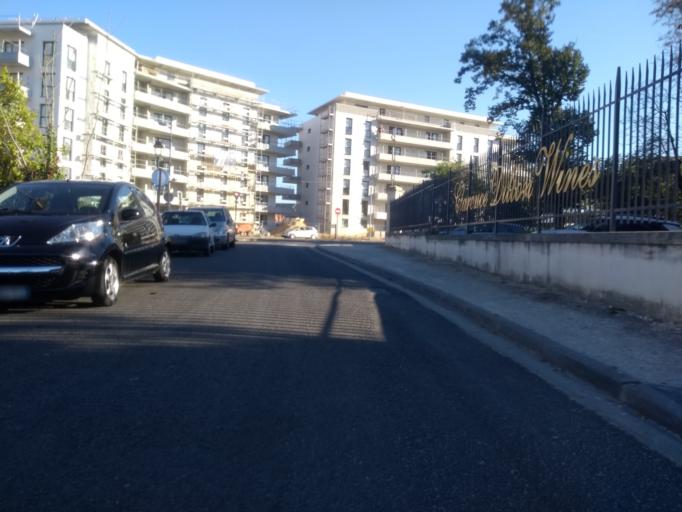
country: FR
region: Aquitaine
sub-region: Departement de la Gironde
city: Talence
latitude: 44.8178
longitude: -0.6023
